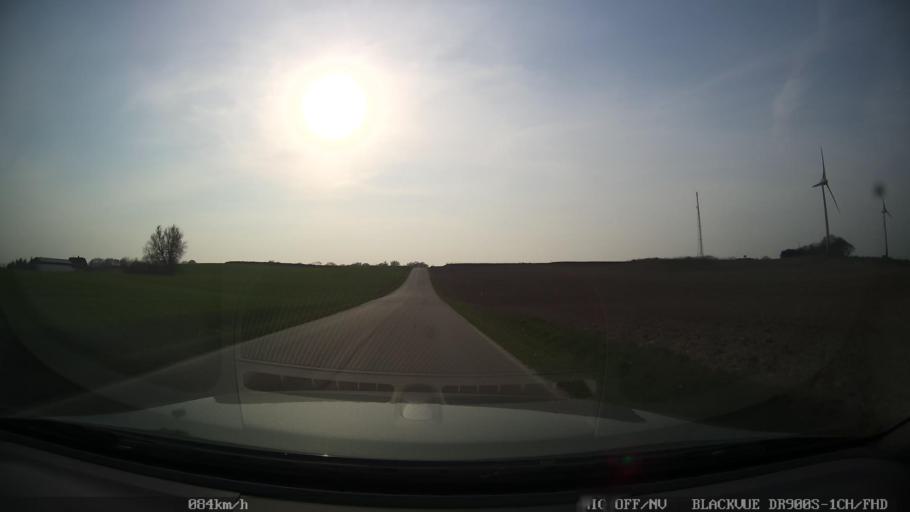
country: SE
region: Skane
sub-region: Ystads Kommun
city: Ystad
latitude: 55.4601
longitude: 13.7914
